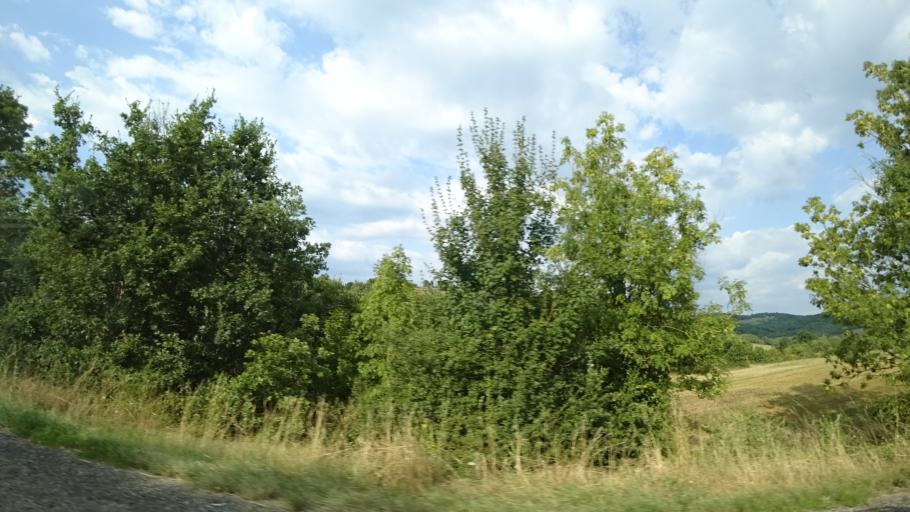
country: FR
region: Midi-Pyrenees
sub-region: Departement de l'Aveyron
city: Saint-Christophe-Vallon
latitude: 44.4823
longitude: 2.4024
